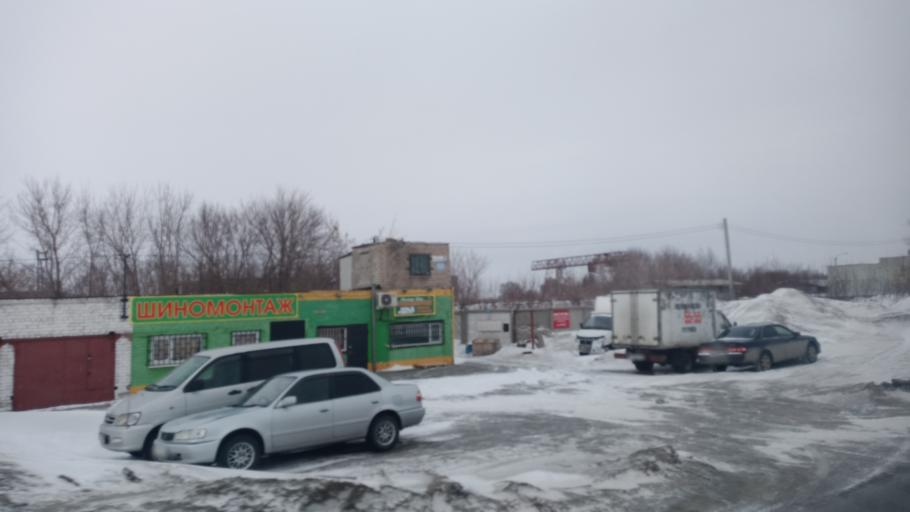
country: RU
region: Altai Krai
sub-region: Gorod Barnaulskiy
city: Barnaul
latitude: 53.3899
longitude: 83.6742
